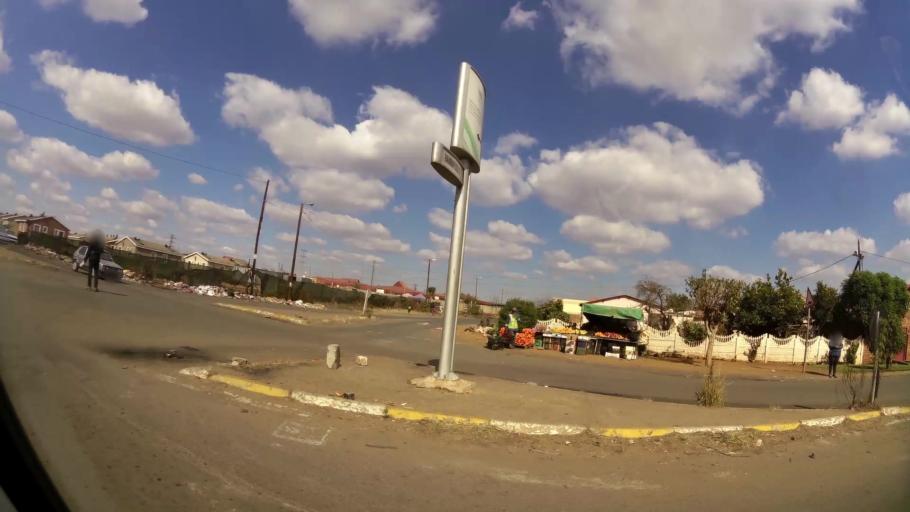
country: ZA
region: Gauteng
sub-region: City of Tshwane Metropolitan Municipality
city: Cullinan
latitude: -25.7111
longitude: 28.4015
